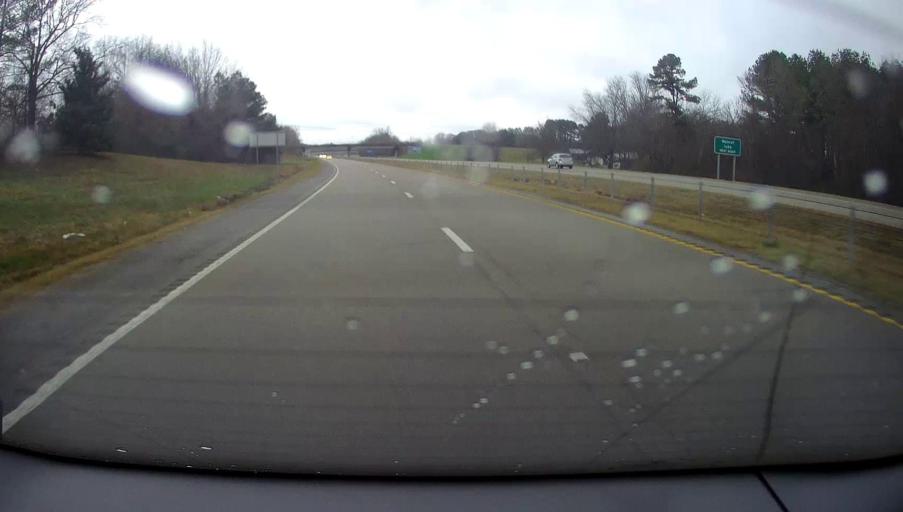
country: US
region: Mississippi
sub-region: Alcorn County
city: Corinth
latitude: 34.9216
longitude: -88.5431
